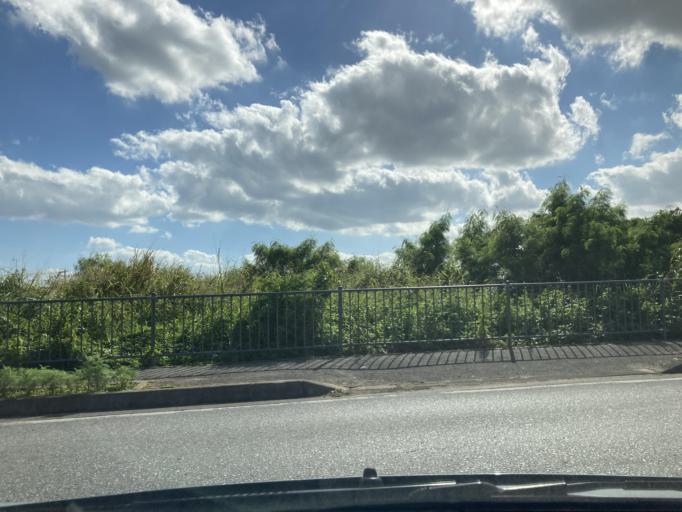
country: JP
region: Okinawa
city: Gushikawa
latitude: 26.3491
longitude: 127.8508
